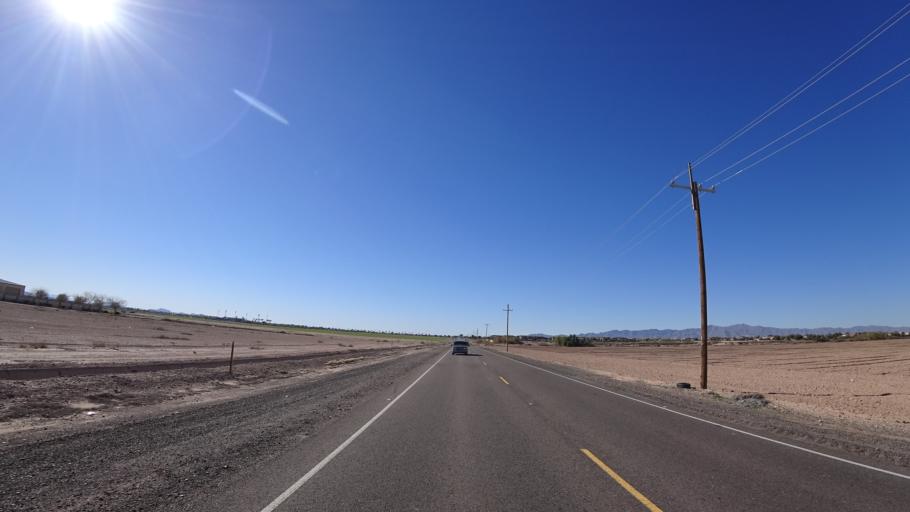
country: US
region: Arizona
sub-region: Maricopa County
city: Goodyear
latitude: 33.4355
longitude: -112.3785
